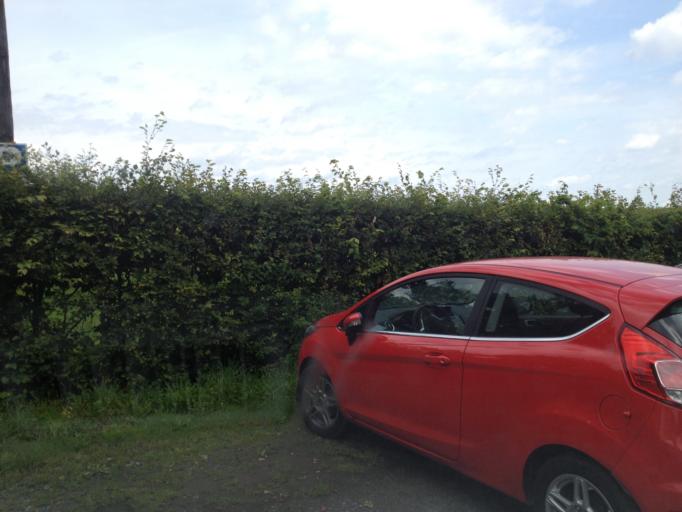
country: DE
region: Saxony
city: Ottendorf-Okrilla
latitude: 51.1585
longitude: 13.8226
